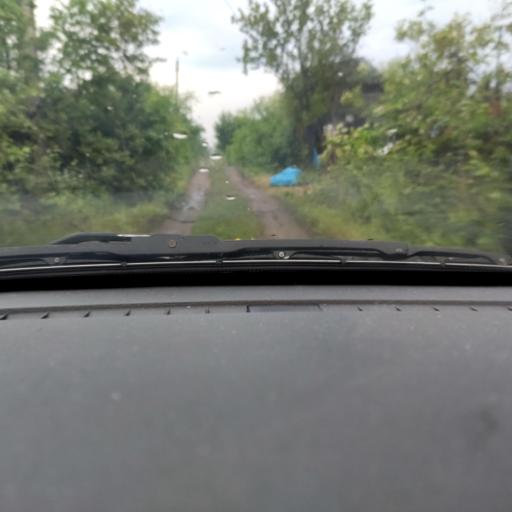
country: RU
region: Voronezj
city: Maslovka
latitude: 51.4912
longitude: 39.2170
